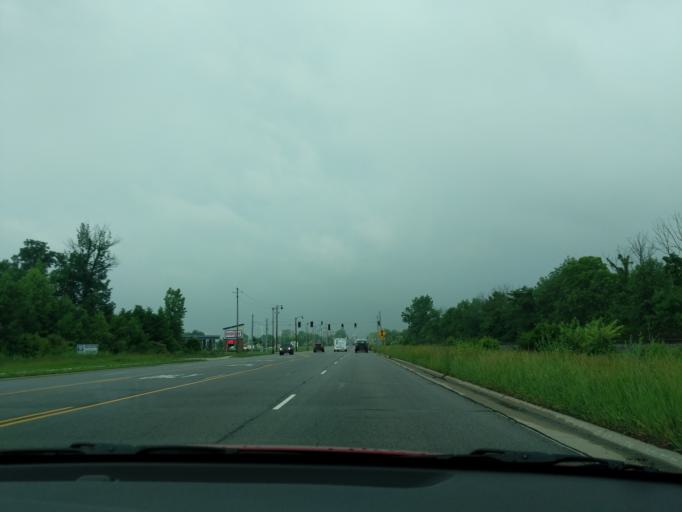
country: US
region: Indiana
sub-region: Hancock County
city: McCordsville
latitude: 39.8891
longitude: -85.9340
